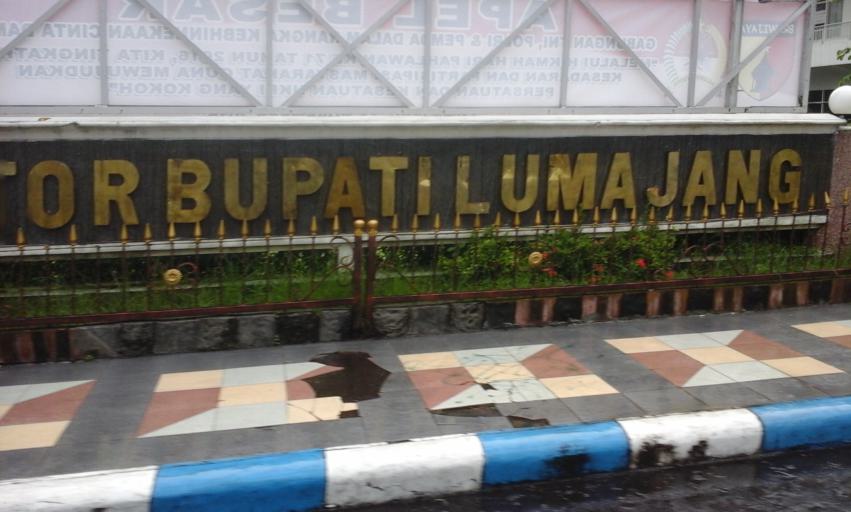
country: ID
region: East Java
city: Lumajang
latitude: -8.1344
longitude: 113.2247
